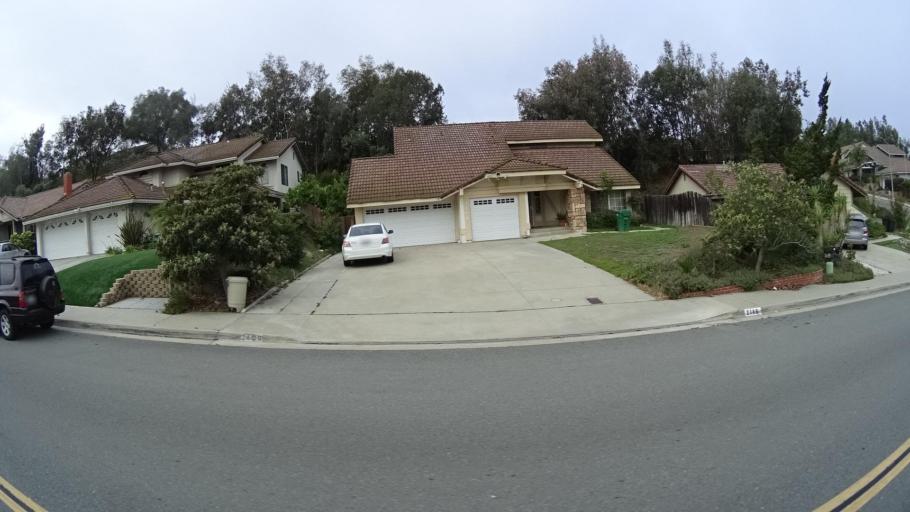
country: US
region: California
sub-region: San Diego County
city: Rancho San Diego
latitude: 32.7523
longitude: -116.9180
